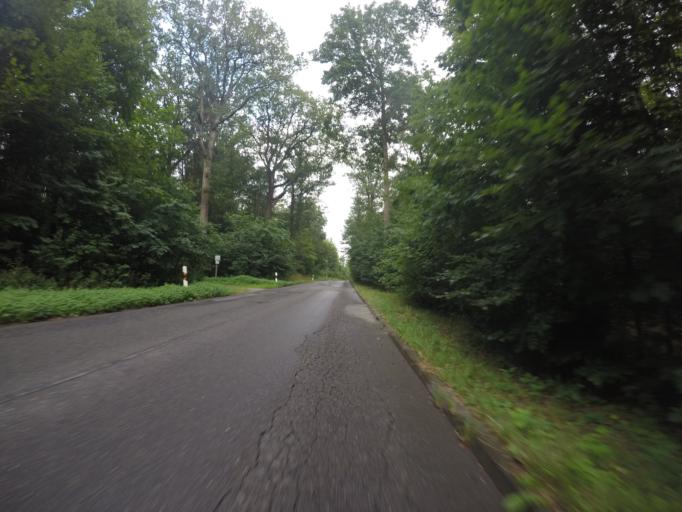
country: DE
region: Baden-Wuerttemberg
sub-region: Regierungsbezirk Stuttgart
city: Stuttgart
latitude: 48.7428
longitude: 9.1938
